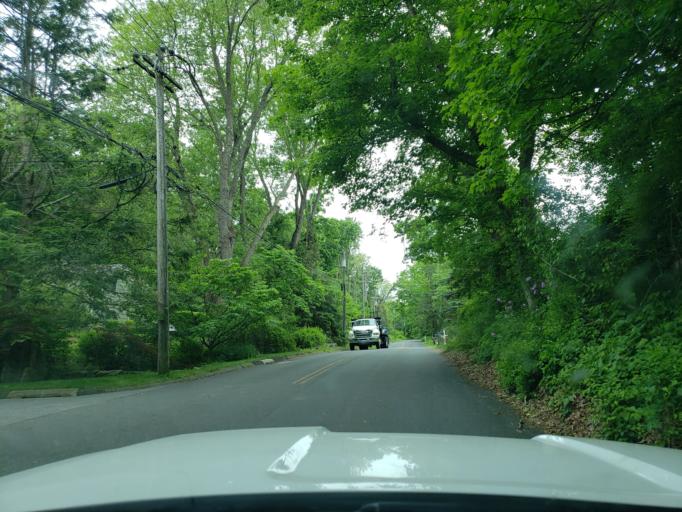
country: US
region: Connecticut
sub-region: Fairfield County
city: Georgetown
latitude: 41.2545
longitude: -73.4368
